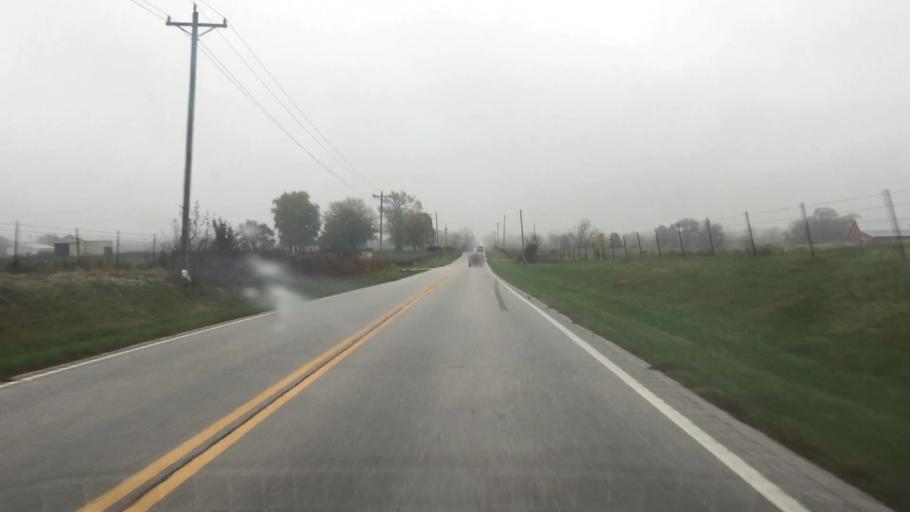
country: US
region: Missouri
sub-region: Callaway County
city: Fulton
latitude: 38.8739
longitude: -92.0597
